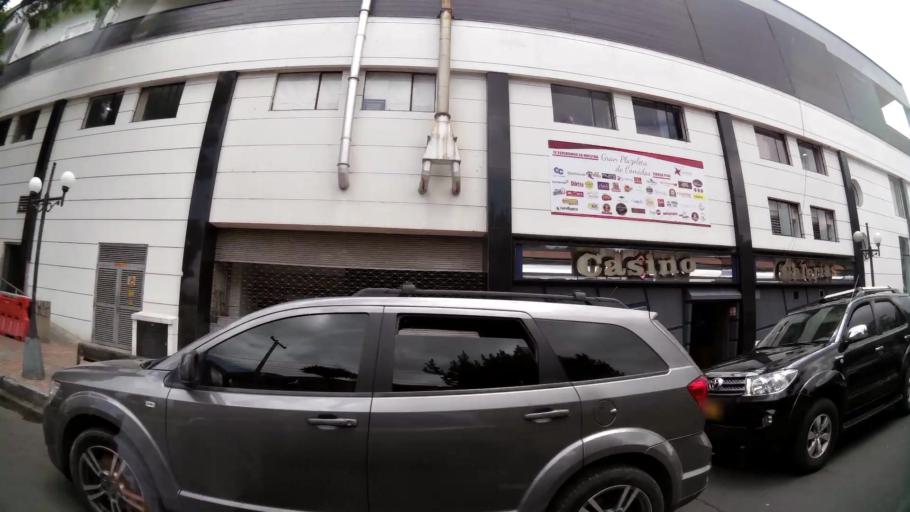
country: CO
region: Bogota D.C.
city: Bogota
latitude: 4.6433
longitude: -74.0750
